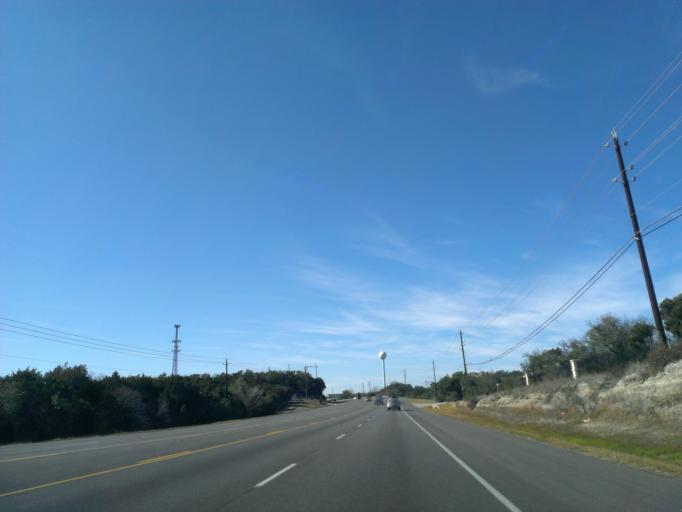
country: US
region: Texas
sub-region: Travis County
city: Lakeway
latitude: 30.3588
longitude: -97.9557
